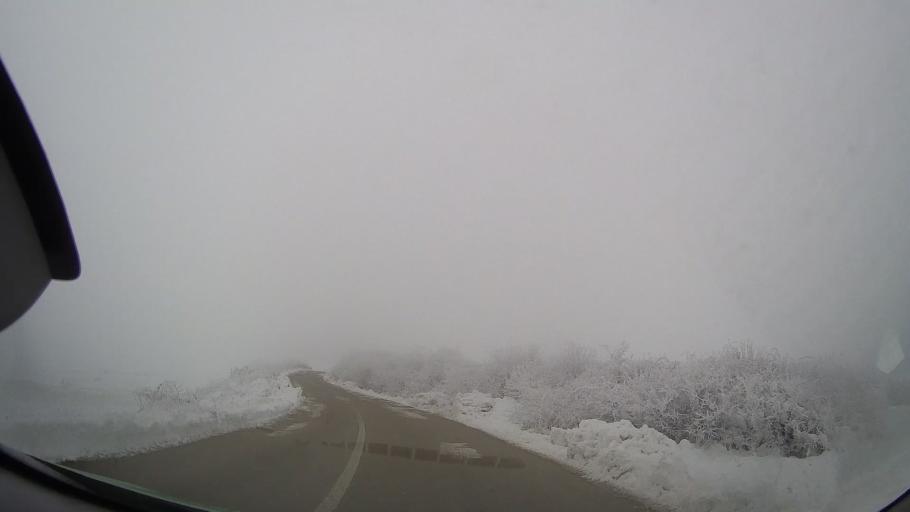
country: RO
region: Iasi
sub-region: Comuna Dagata
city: Dagata
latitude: 46.9223
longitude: 27.1753
